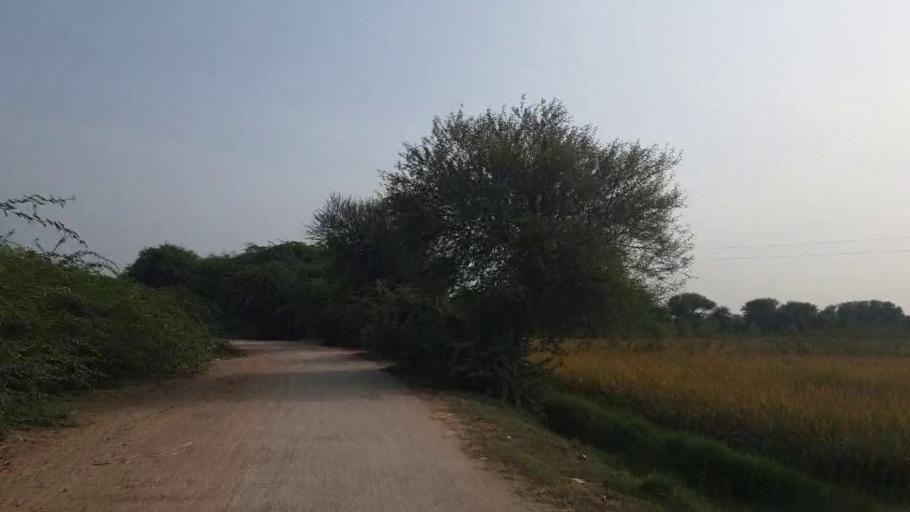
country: PK
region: Sindh
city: Badin
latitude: 24.6103
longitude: 68.6862
